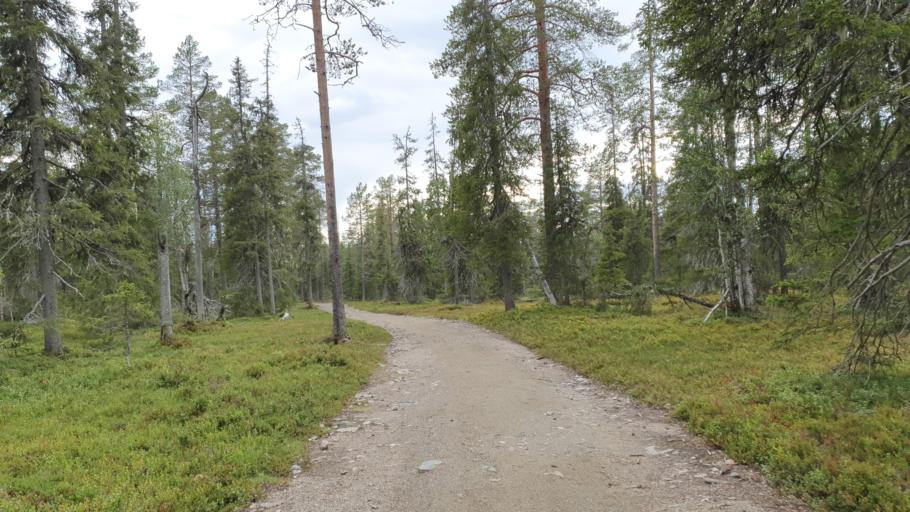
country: FI
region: Lapland
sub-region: Tunturi-Lappi
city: Kolari
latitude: 67.6182
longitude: 24.2418
